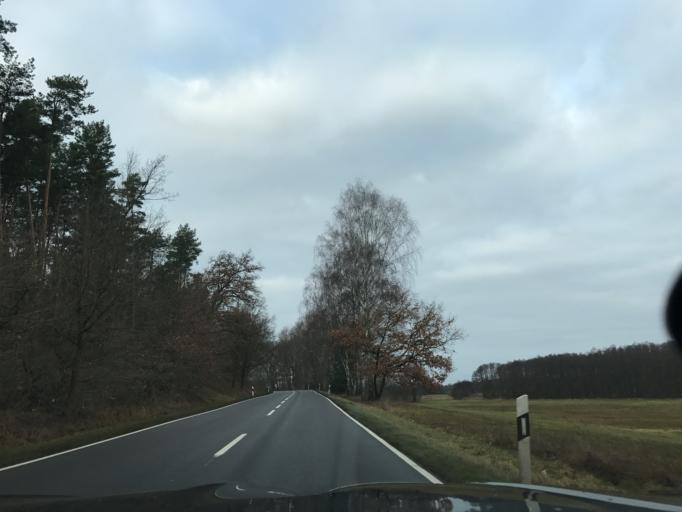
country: DE
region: Brandenburg
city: Brandenburg an der Havel
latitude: 52.3576
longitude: 12.6050
